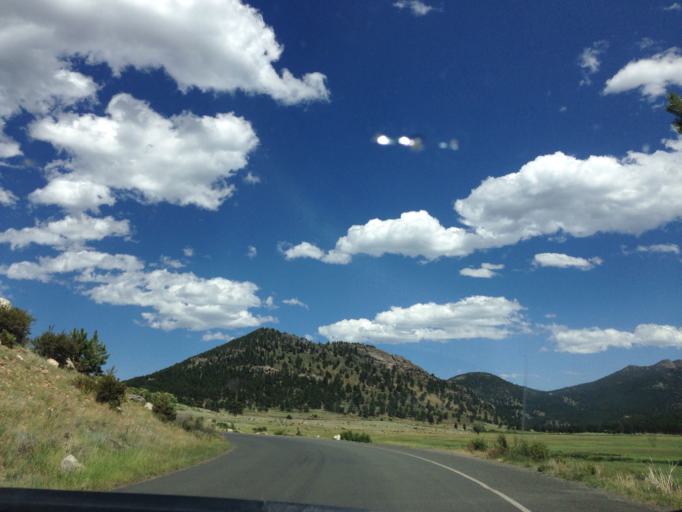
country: US
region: Colorado
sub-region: Larimer County
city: Estes Park
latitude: 40.3565
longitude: -105.5983
